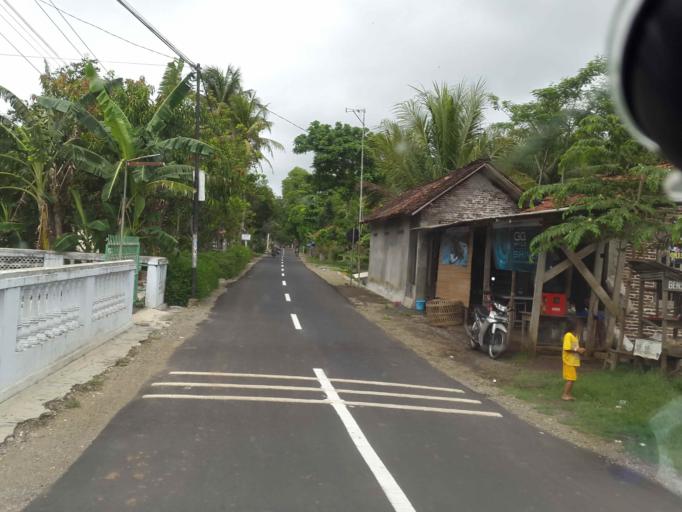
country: ID
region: Central Java
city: Kutoarjo
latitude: -7.7322
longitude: 109.9760
